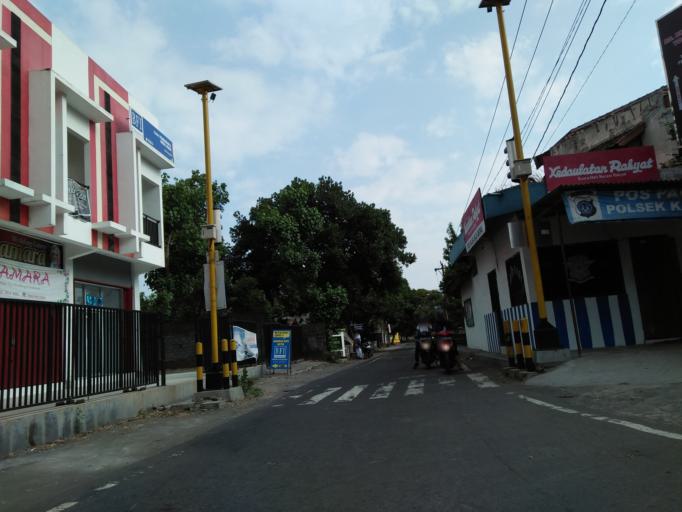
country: ID
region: Central Java
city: Candi Prambanan
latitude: -7.7575
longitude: 110.4804
